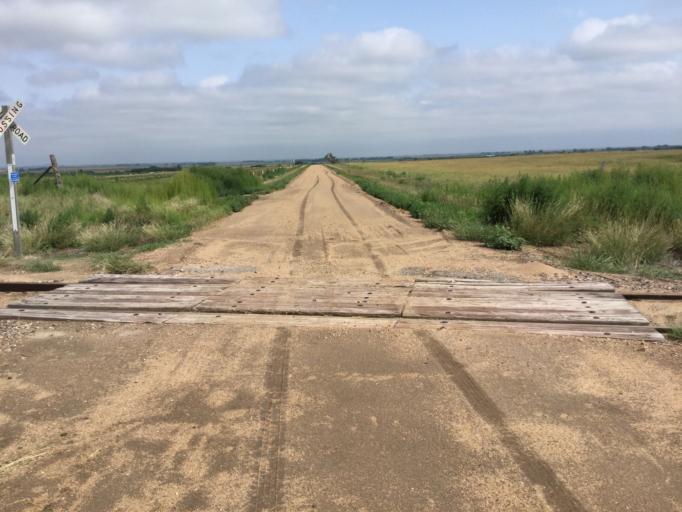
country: US
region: Kansas
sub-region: Rush County
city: La Crosse
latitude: 38.5688
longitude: -99.5313
